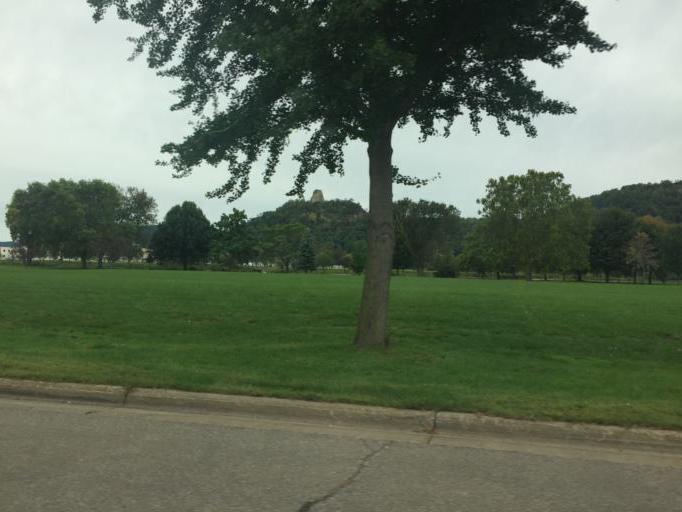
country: US
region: Minnesota
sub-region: Winona County
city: Winona
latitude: 44.0382
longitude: -91.6253
